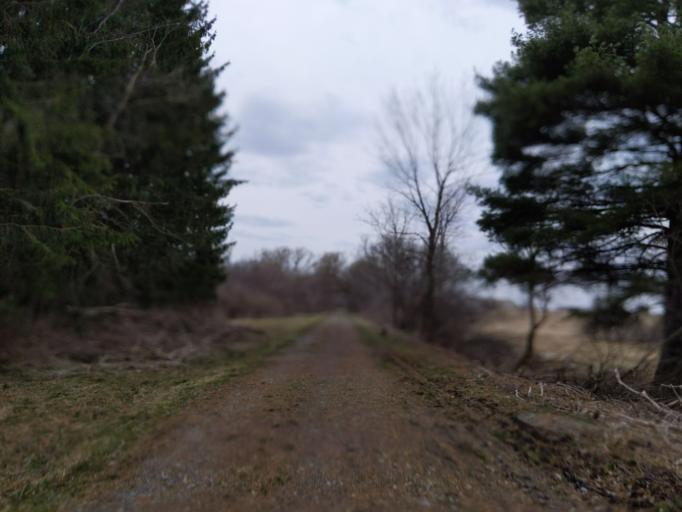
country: US
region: New York
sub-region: Tompkins County
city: Dryden
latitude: 42.5014
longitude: -76.3361
